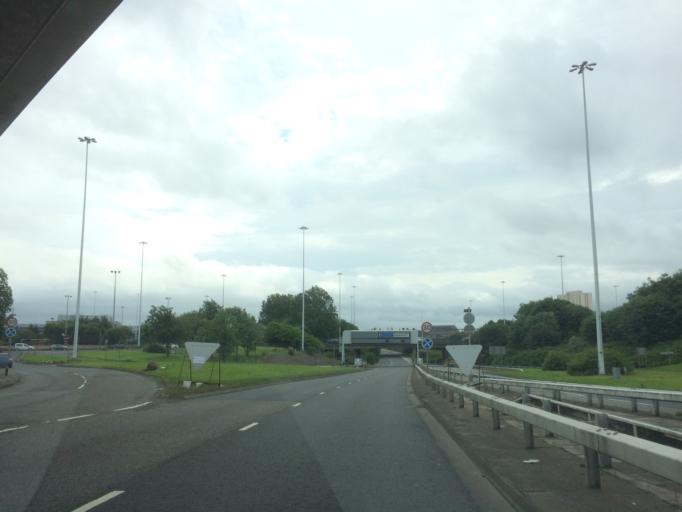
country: GB
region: Scotland
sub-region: Glasgow City
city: Glasgow
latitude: 55.8703
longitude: -4.2340
